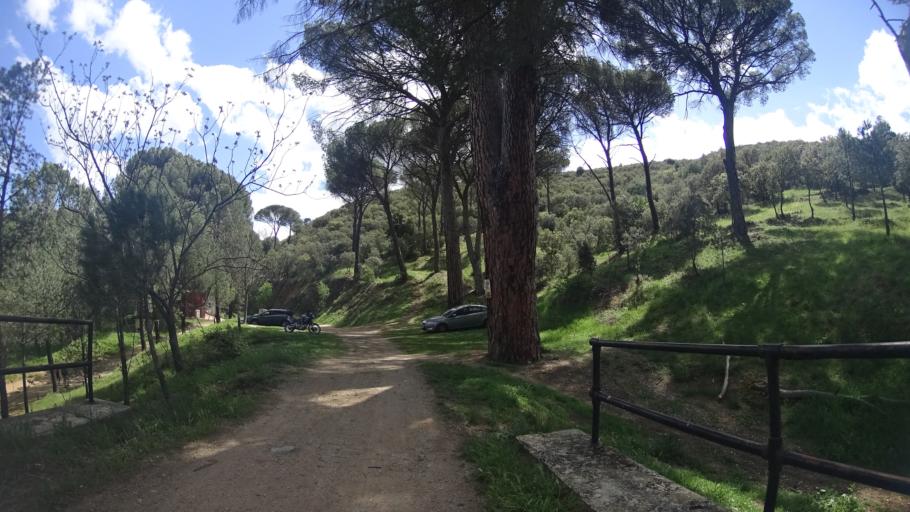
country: ES
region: Madrid
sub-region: Provincia de Madrid
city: Pelayos de la Presa
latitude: 40.3655
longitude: -4.3048
